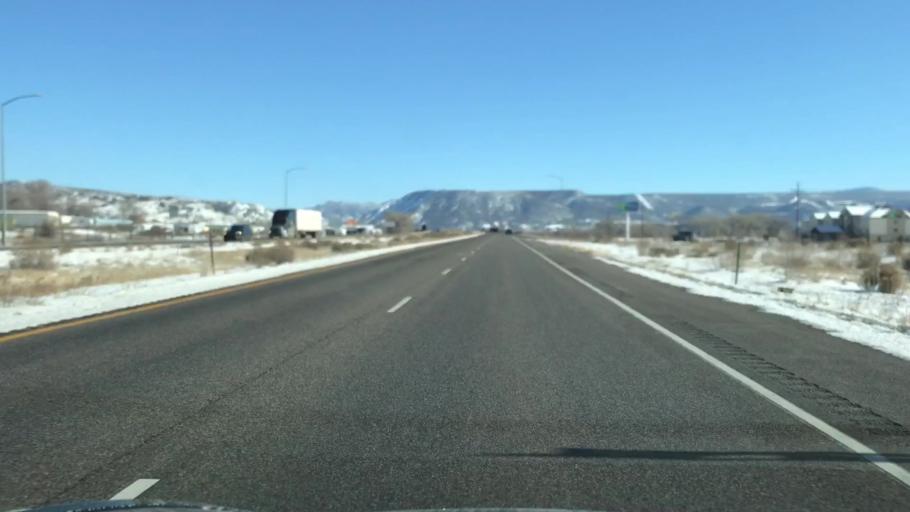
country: US
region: Colorado
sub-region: Garfield County
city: Silt
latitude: 39.5445
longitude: -107.6514
